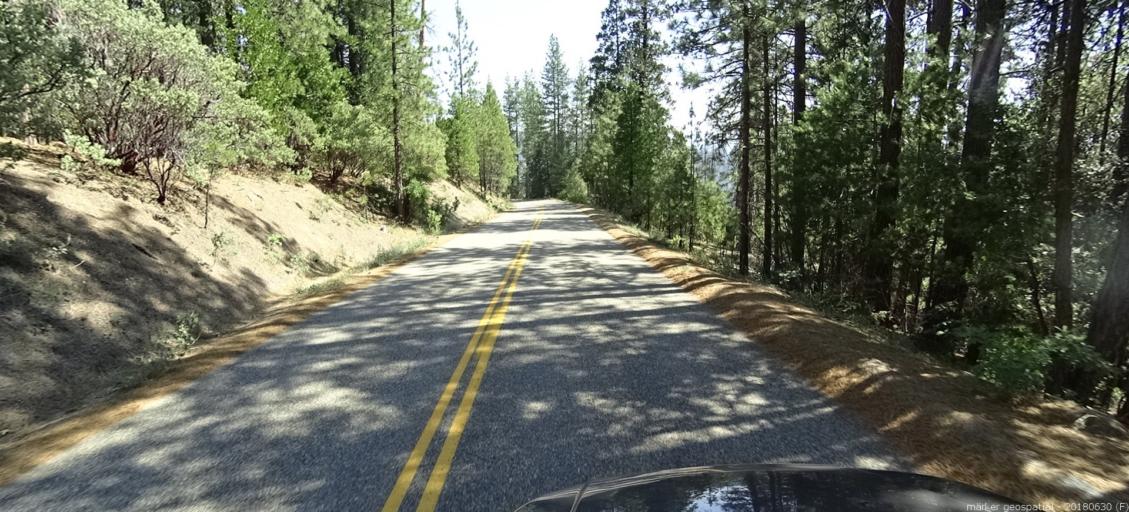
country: US
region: California
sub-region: Madera County
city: Oakhurst
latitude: 37.3682
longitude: -119.3900
